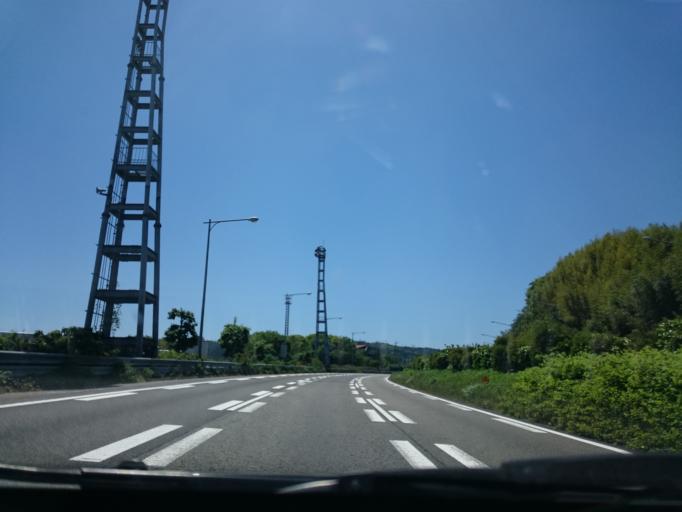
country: JP
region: Kanagawa
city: Hadano
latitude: 35.3438
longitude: 139.2035
